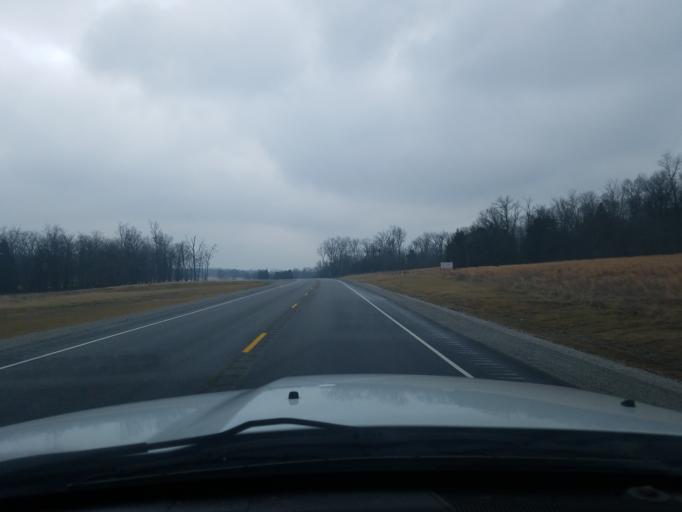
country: US
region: Kentucky
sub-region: Logan County
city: Russellville
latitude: 36.8139
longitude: -86.8998
